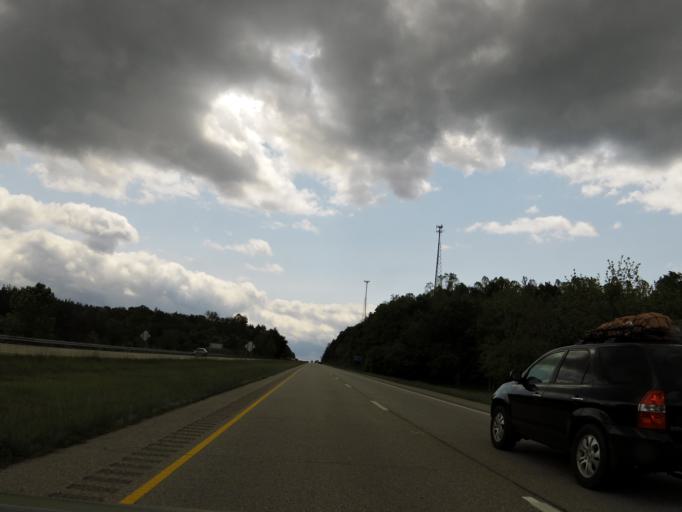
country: US
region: Ohio
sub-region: Meigs County
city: Pomeroy
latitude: 39.1353
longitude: -82.0212
